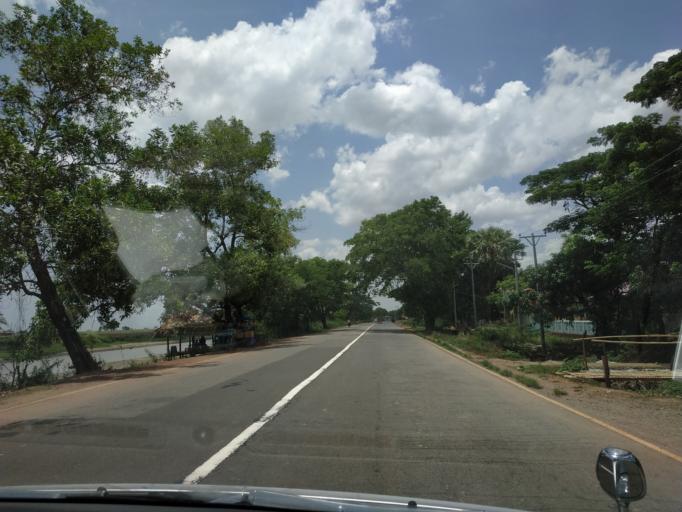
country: MM
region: Bago
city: Thanatpin
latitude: 17.5142
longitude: 96.7163
